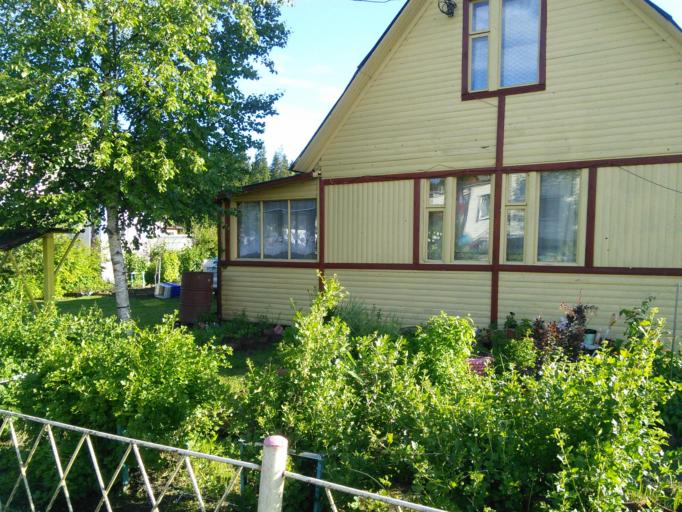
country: RU
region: Republic of Karelia
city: Shuya
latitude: 61.8500
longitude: 34.1434
